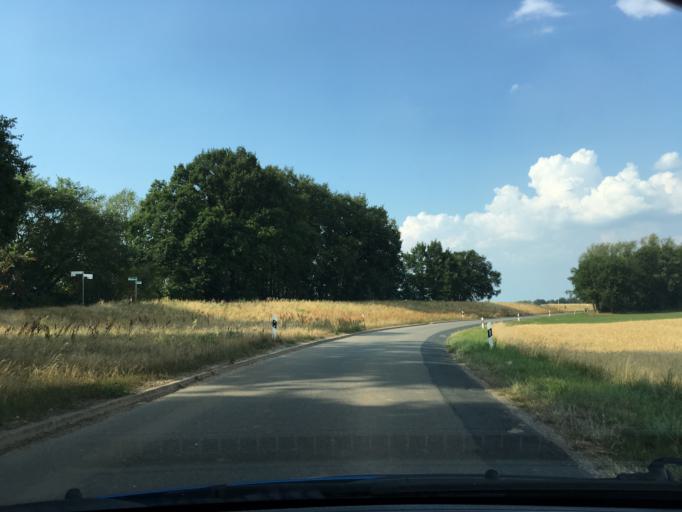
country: DE
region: Lower Saxony
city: Damnatz
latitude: 53.1474
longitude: 11.1201
